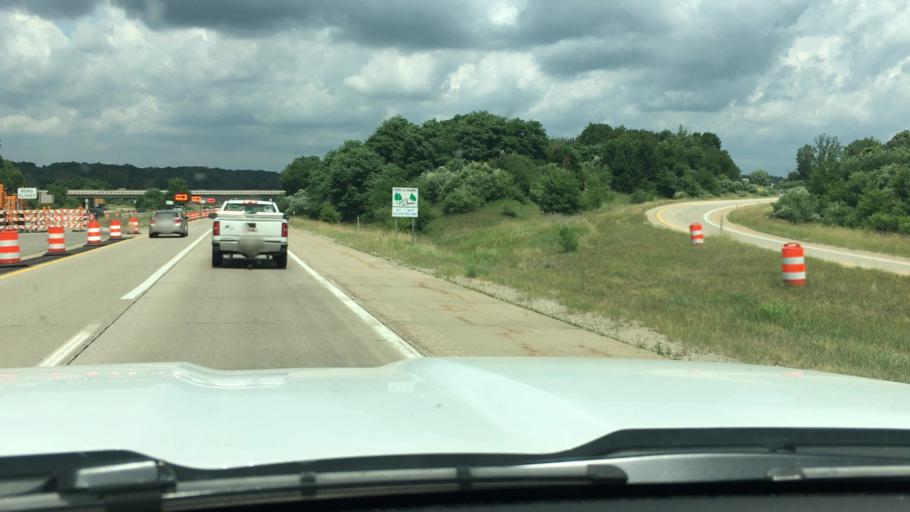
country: US
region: Michigan
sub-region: Kent County
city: Rockford
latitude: 43.1138
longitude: -85.6079
